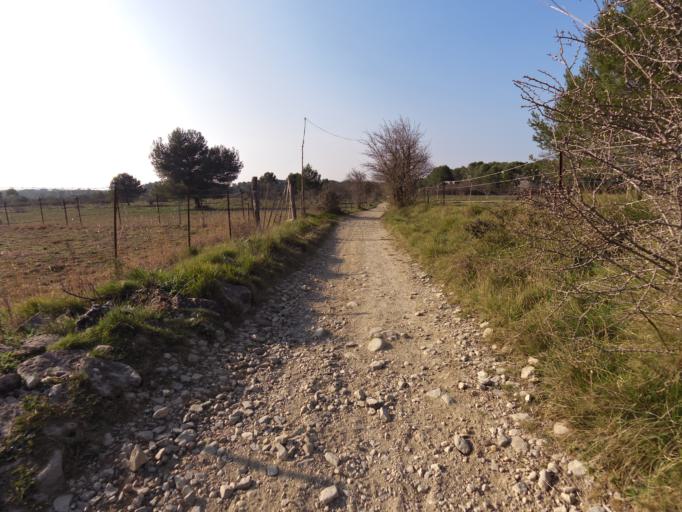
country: FR
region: Languedoc-Roussillon
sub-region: Departement du Gard
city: Gallargues-le-Montueux
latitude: 43.7305
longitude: 4.1637
